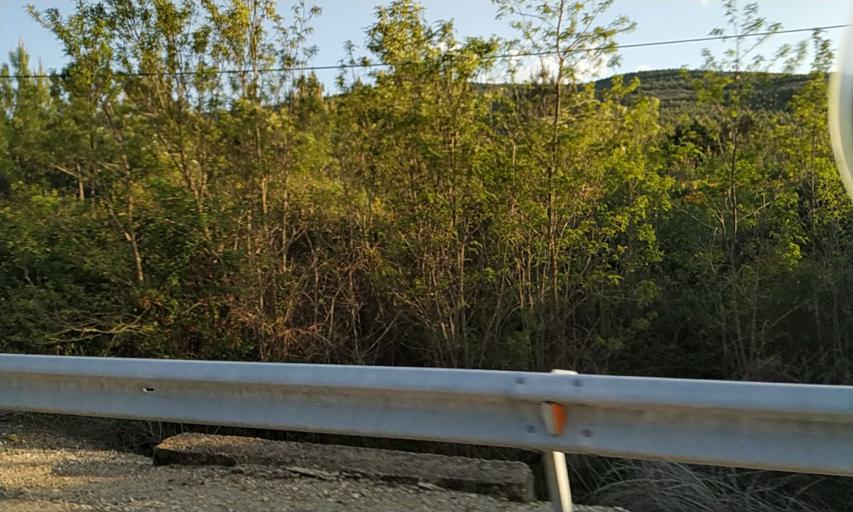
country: PT
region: Portalegre
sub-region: Portalegre
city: Sao Juliao
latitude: 39.3489
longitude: -7.3024
